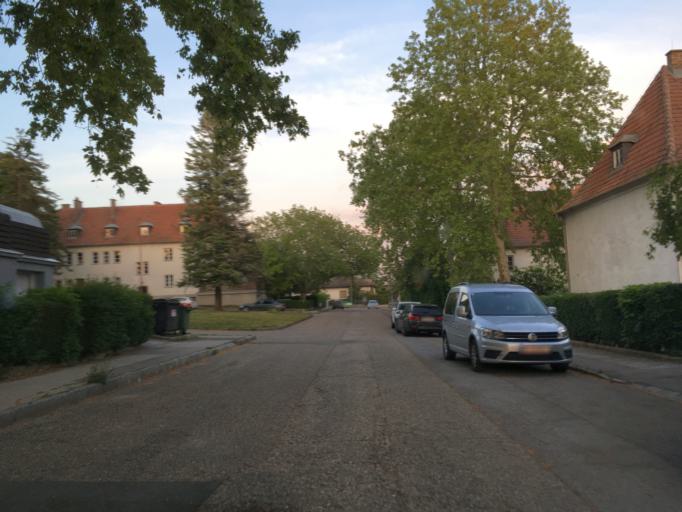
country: AT
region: Lower Austria
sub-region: Politischer Bezirk Korneuburg
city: Stockerau
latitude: 48.3913
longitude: 16.2016
